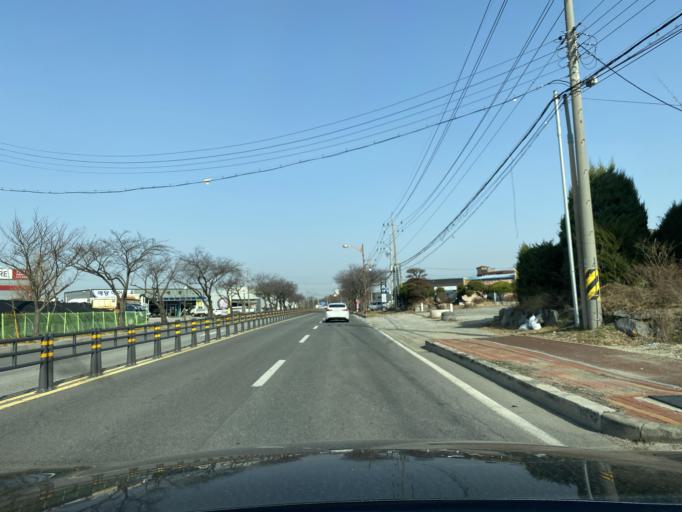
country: KR
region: Chungcheongnam-do
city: Yesan
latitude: 36.7089
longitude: 126.8401
